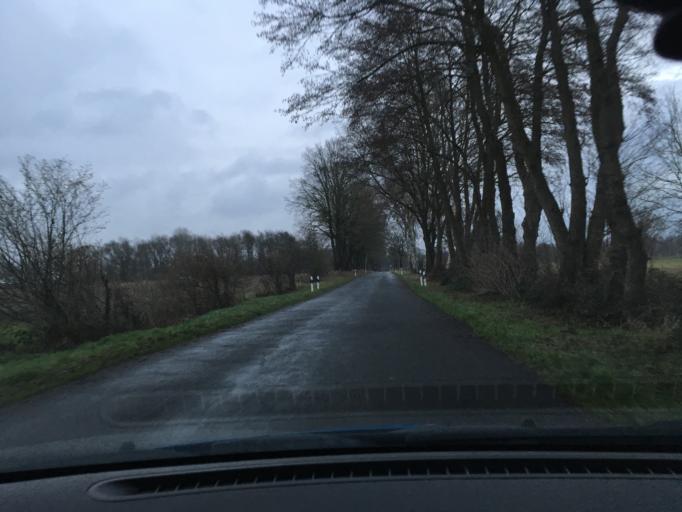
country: DE
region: Mecklenburg-Vorpommern
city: Nostorf
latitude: 53.4051
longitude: 10.6607
